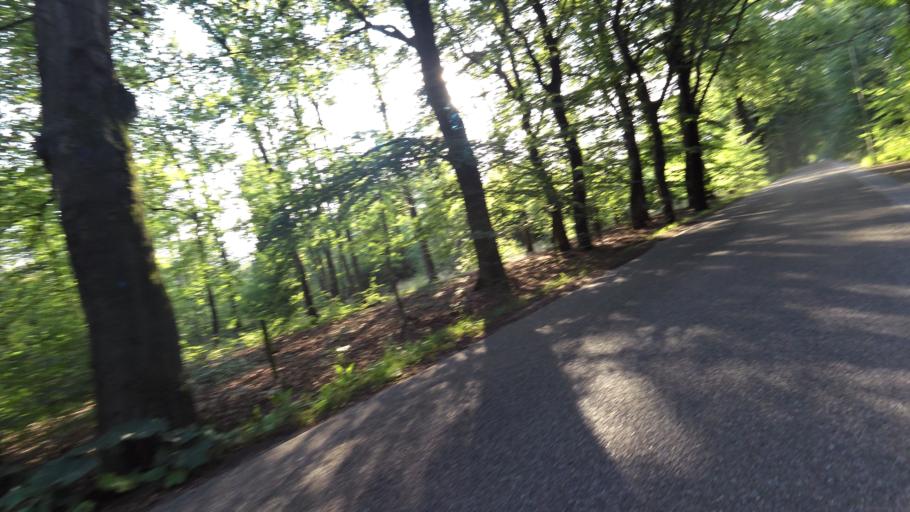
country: NL
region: Gelderland
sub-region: Gemeente Renkum
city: Wolfheze
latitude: 52.0177
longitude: 5.8251
